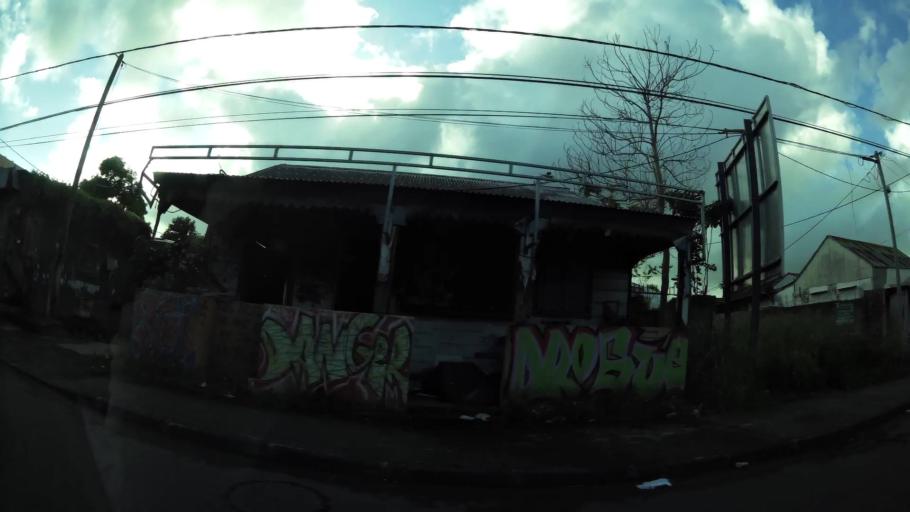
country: GP
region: Guadeloupe
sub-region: Guadeloupe
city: Pointe-a-Pitre
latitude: 16.2496
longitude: -61.5299
